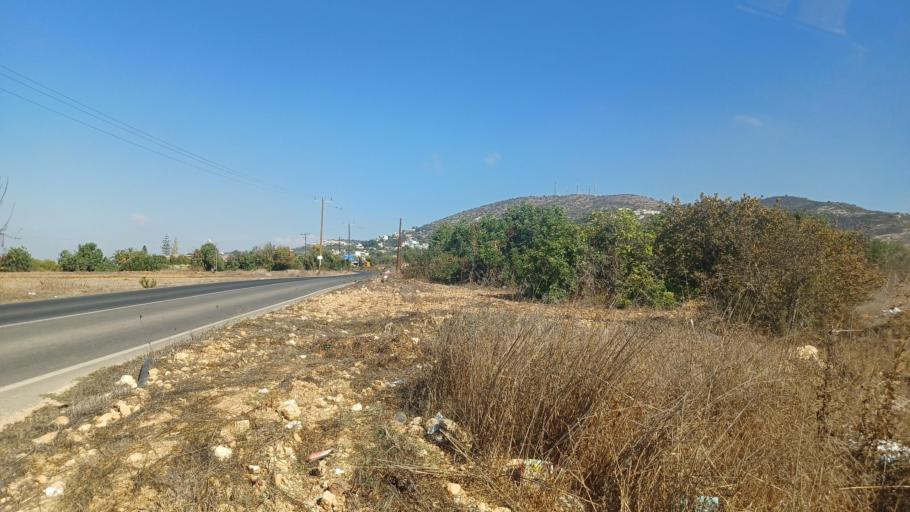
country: CY
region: Pafos
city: Mesogi
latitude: 34.8258
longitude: 32.4471
